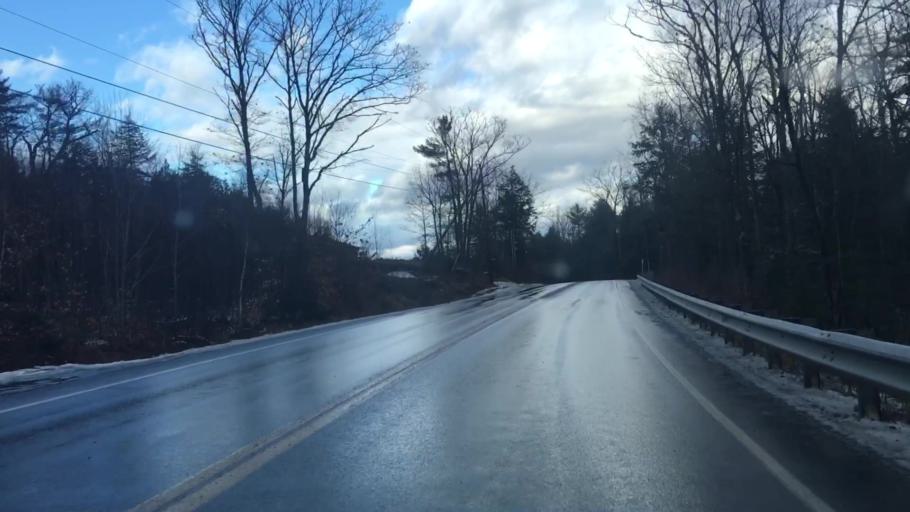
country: US
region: Maine
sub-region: Hancock County
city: Dedham
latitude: 44.6331
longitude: -68.7007
